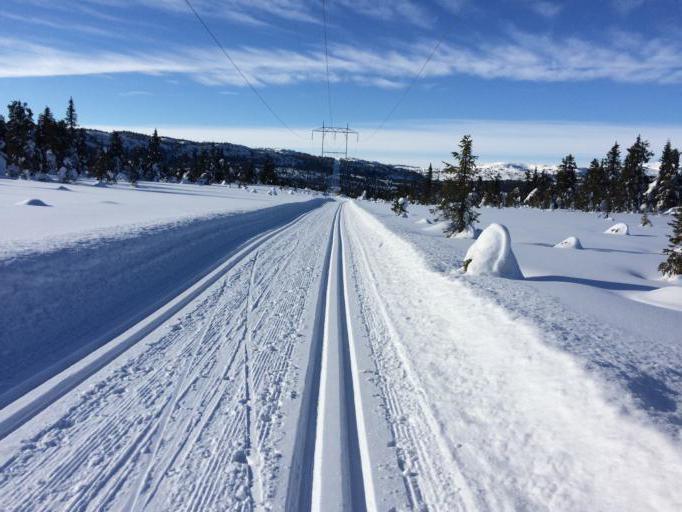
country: NO
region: Oppland
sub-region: Gausdal
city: Segalstad bru
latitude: 61.3173
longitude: 10.0961
